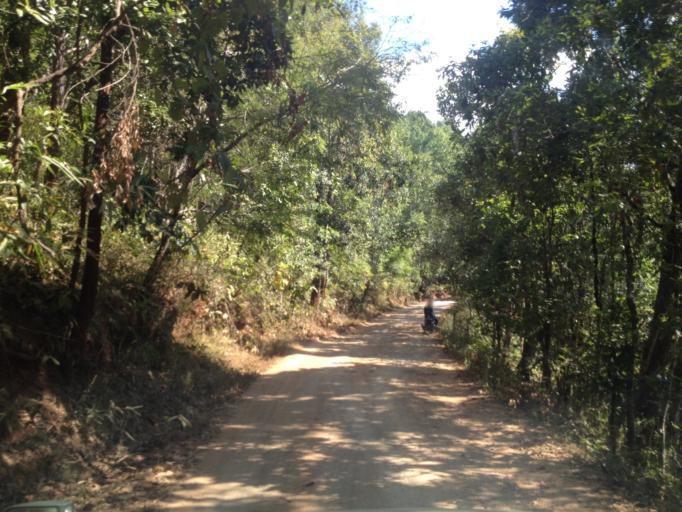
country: TH
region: Mae Hong Son
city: Ban Huai I Huak
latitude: 18.1092
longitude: 98.1665
